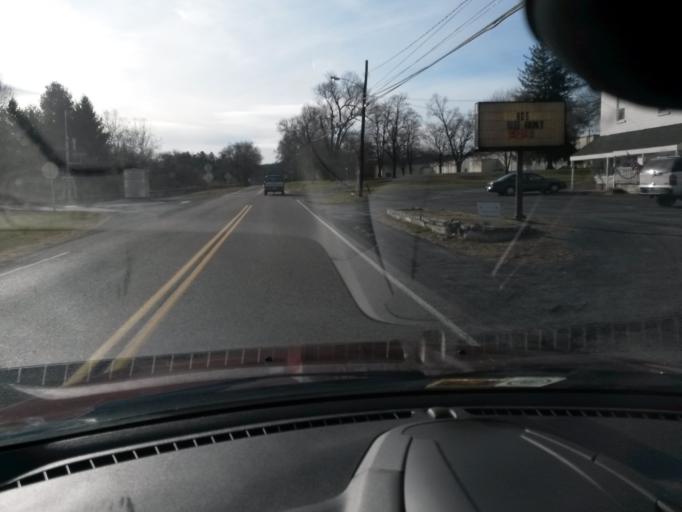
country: US
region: Virginia
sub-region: Rockbridge County
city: East Lexington
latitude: 38.0752
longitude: -79.3905
